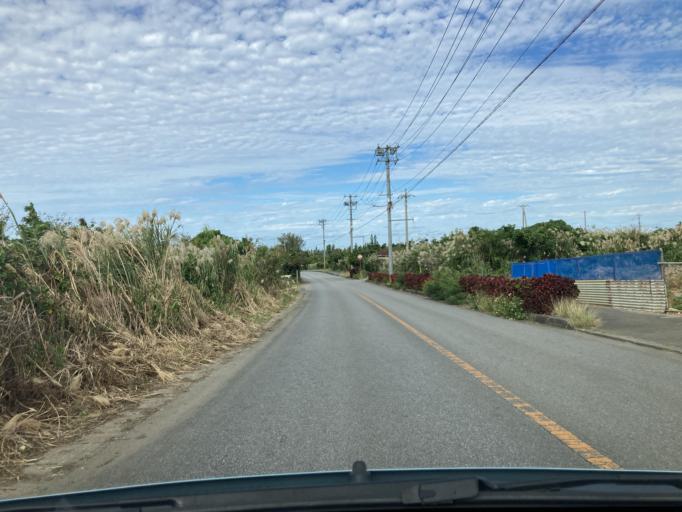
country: JP
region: Okinawa
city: Ishikawa
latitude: 26.4319
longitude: 127.7276
